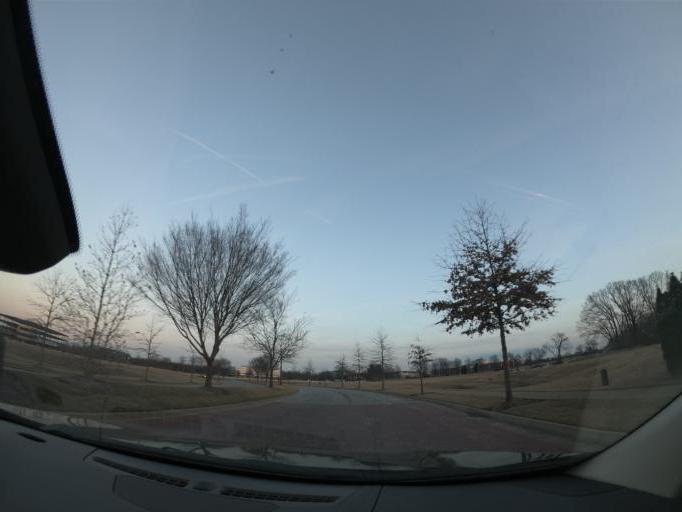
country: US
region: Kentucky
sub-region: Jefferson County
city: Lyndon
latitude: 38.2565
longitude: -85.5867
